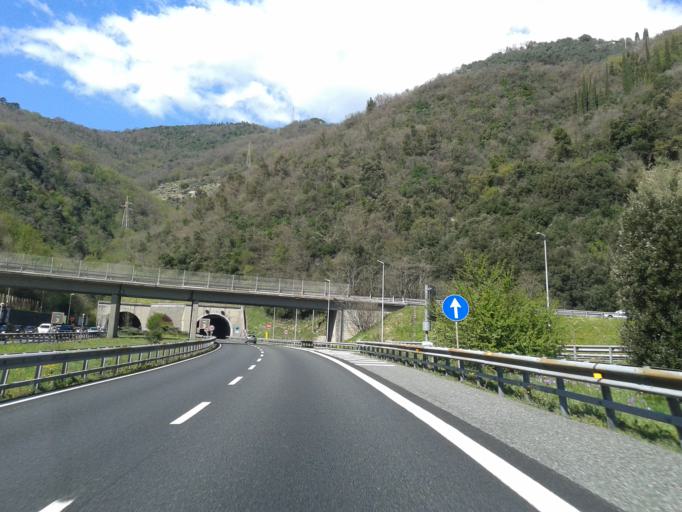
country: IT
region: Liguria
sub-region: Provincia di Genova
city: Avegno
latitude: 44.3771
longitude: 9.1444
